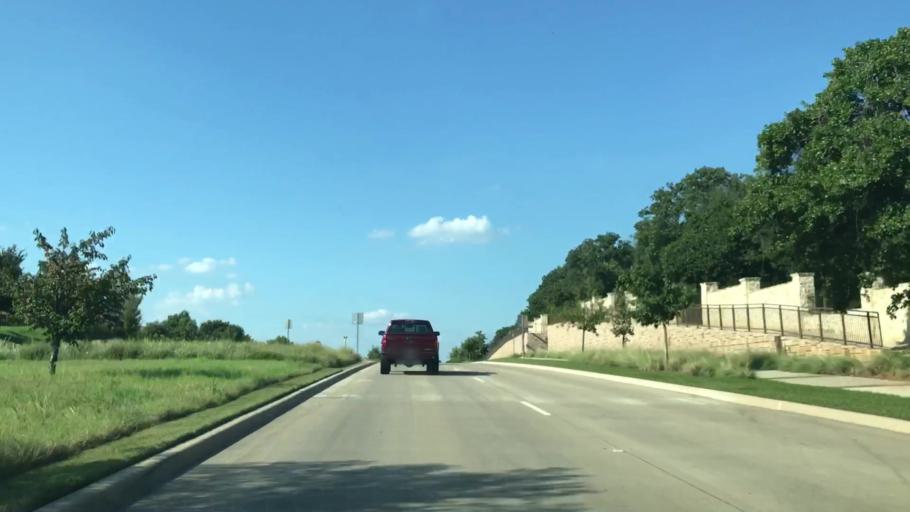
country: US
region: Texas
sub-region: Denton County
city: Trophy Club
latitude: 32.9665
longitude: -97.1857
